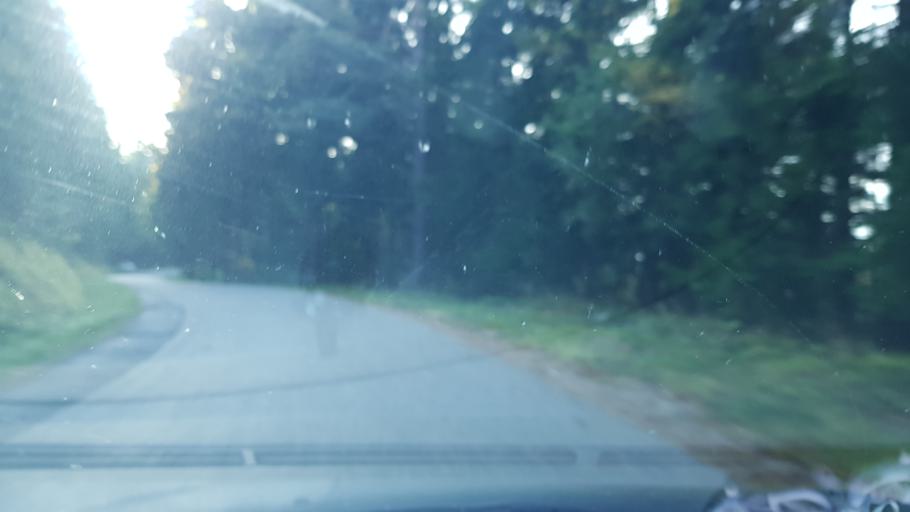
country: SI
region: Slovenj Gradec
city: Legen
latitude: 46.4859
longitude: 15.1598
